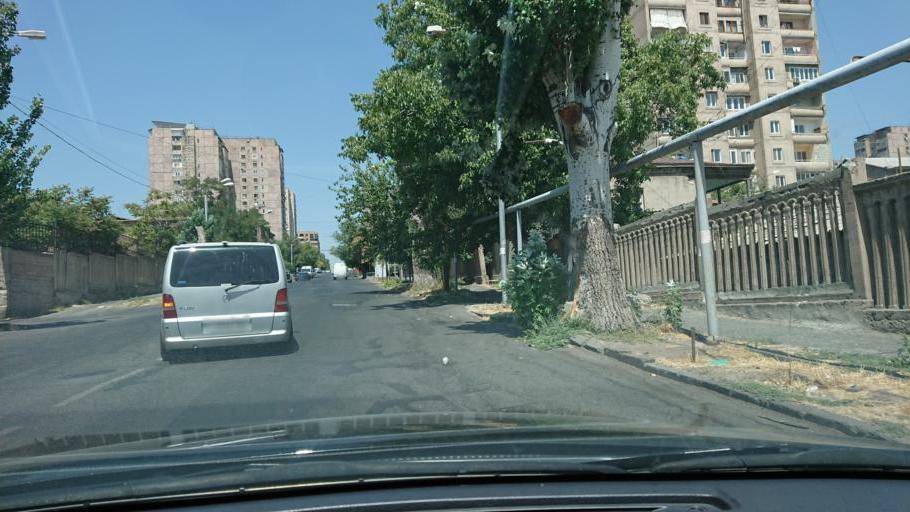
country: AM
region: Yerevan
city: Yerevan
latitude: 40.1954
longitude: 44.5039
